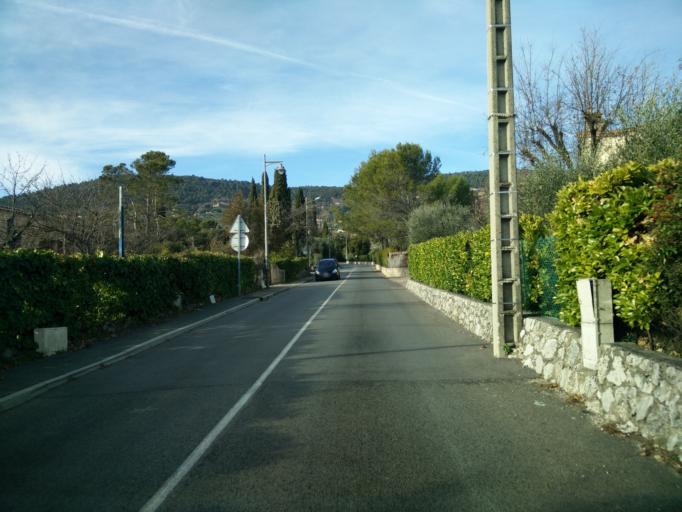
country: FR
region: Provence-Alpes-Cote d'Azur
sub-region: Departement des Alpes-Maritimes
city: Speracedes
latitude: 43.6364
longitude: 6.8580
